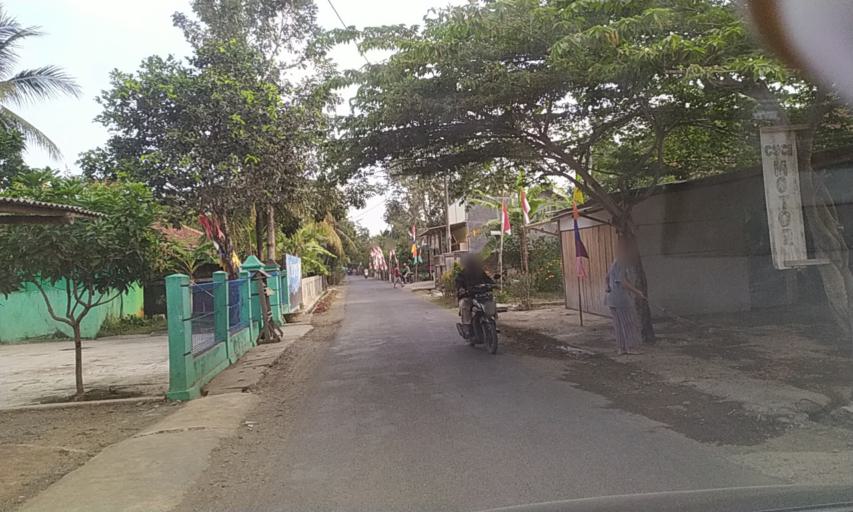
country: ID
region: Central Java
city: Madusari
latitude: -7.6178
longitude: 109.0859
